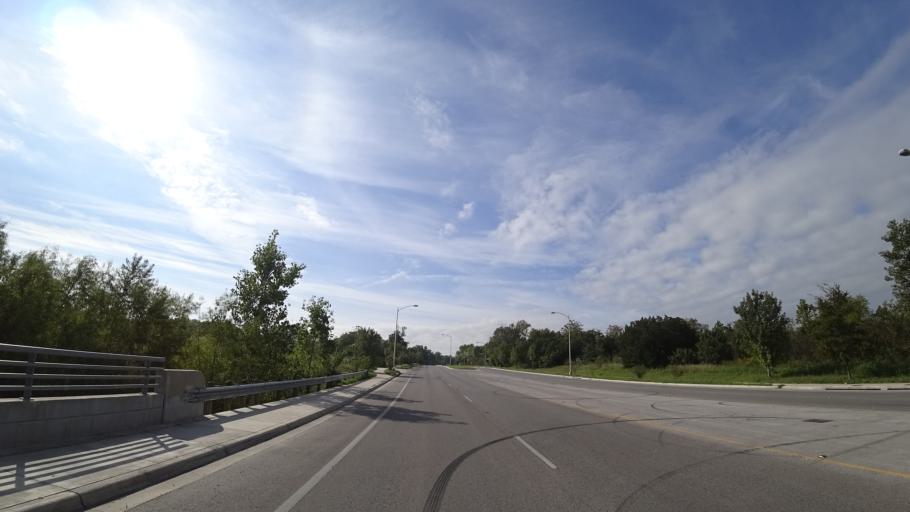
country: US
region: Texas
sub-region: Travis County
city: Austin
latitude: 30.2032
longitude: -97.7421
